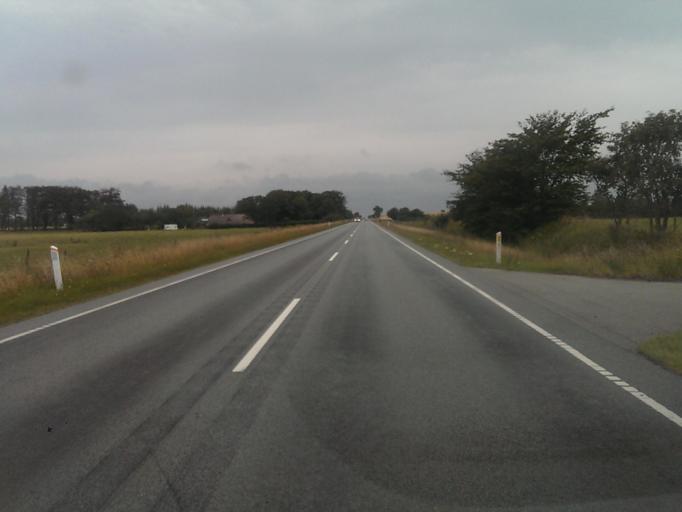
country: DK
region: South Denmark
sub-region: Esbjerg Kommune
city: Tjaereborg
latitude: 55.5404
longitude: 8.6174
